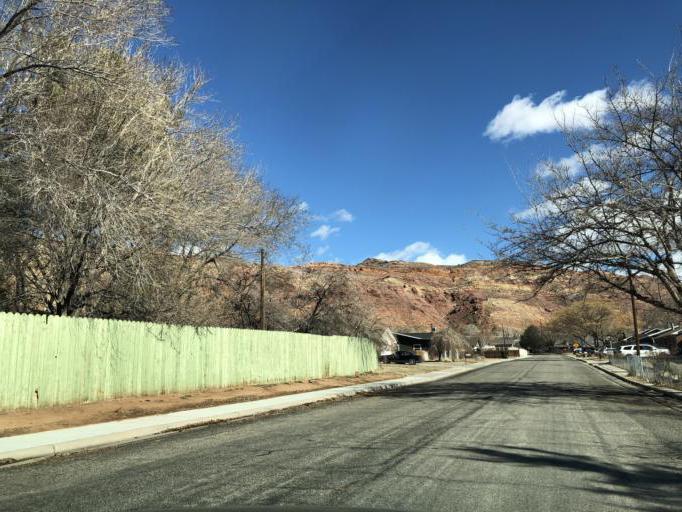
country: US
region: Utah
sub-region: Grand County
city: Moab
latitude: 38.5824
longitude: -109.5576
